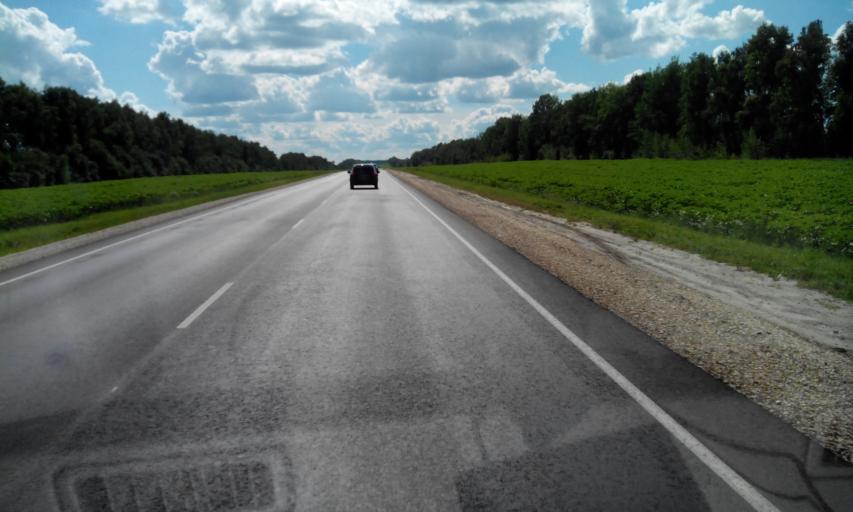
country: RU
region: Penza
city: Bogoslovka
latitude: 53.1381
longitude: 44.4913
